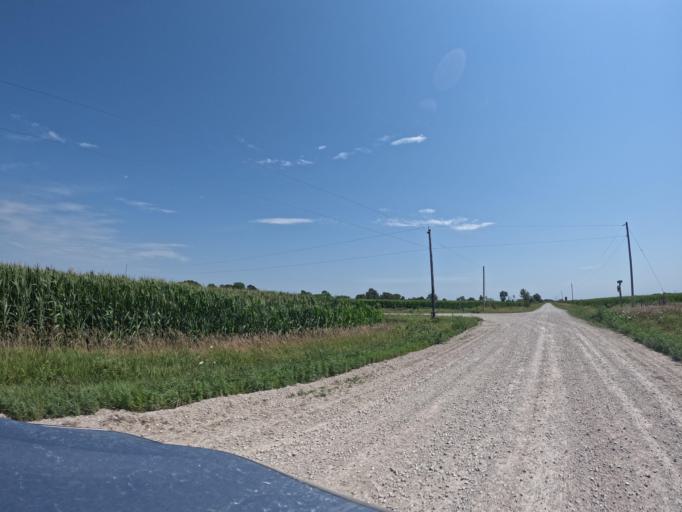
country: US
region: Iowa
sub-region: Henry County
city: Mount Pleasant
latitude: 40.8940
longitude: -91.6317
